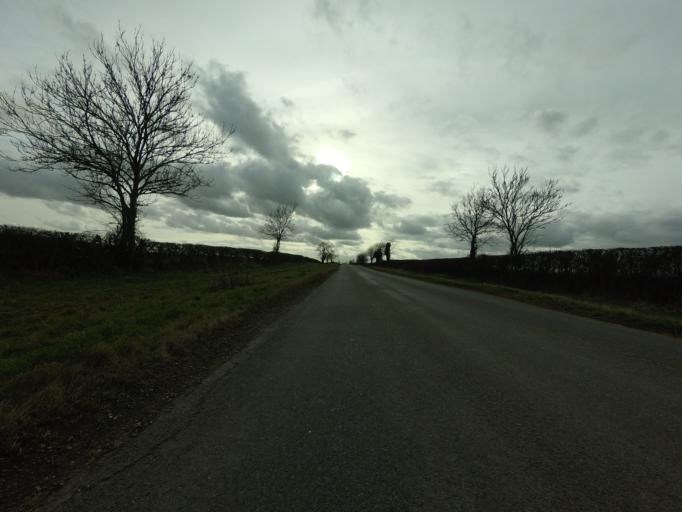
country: GB
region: England
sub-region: Lincolnshire
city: Grantham
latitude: 52.8607
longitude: -0.6388
